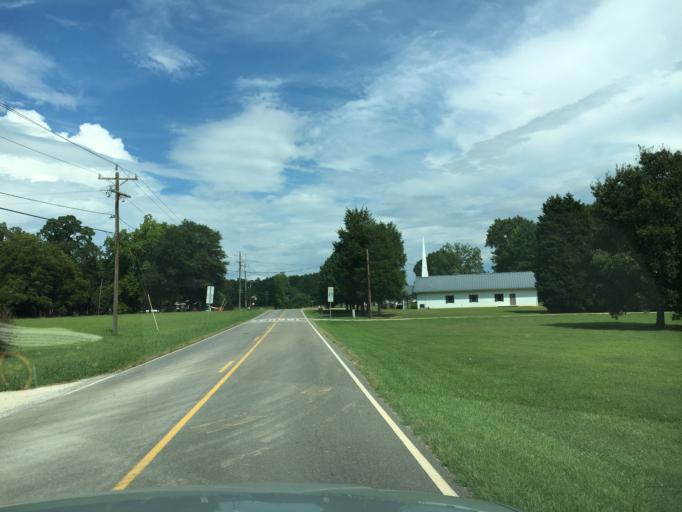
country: US
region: North Carolina
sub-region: Catawba County
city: Claremont
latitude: 35.6301
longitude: -81.1314
